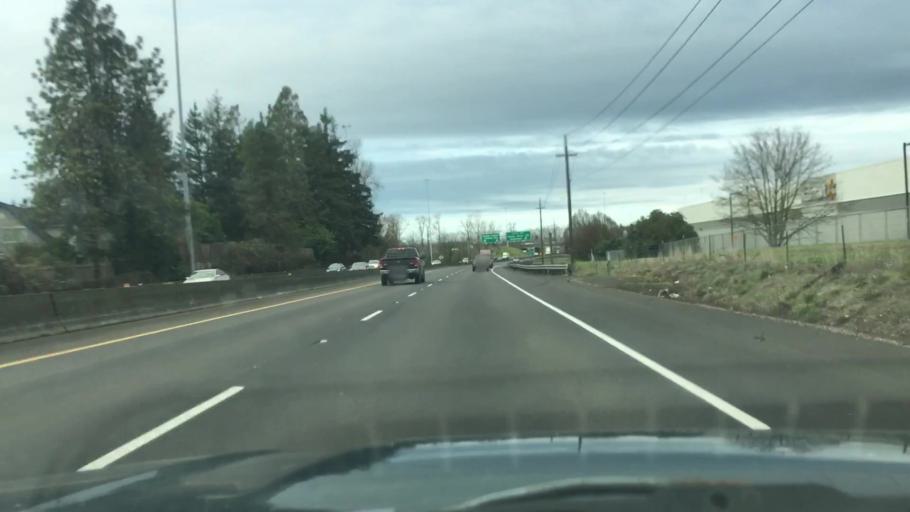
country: US
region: Oregon
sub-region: Lane County
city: Eugene
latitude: 44.0898
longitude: -123.0928
